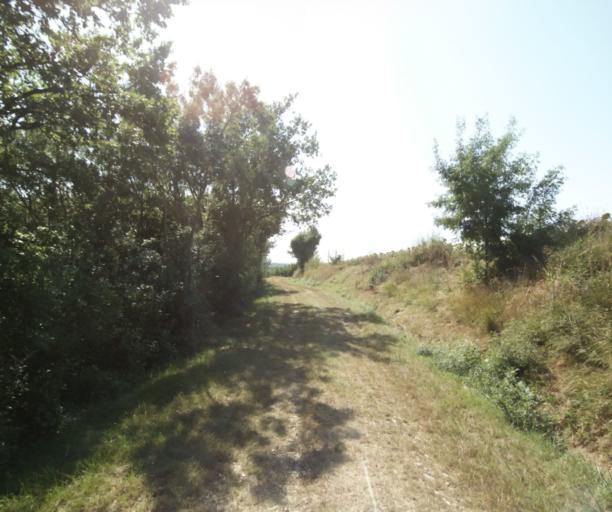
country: FR
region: Midi-Pyrenees
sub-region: Departement de la Haute-Garonne
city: Saint-Felix-Lauragais
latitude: 43.4390
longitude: 1.8404
